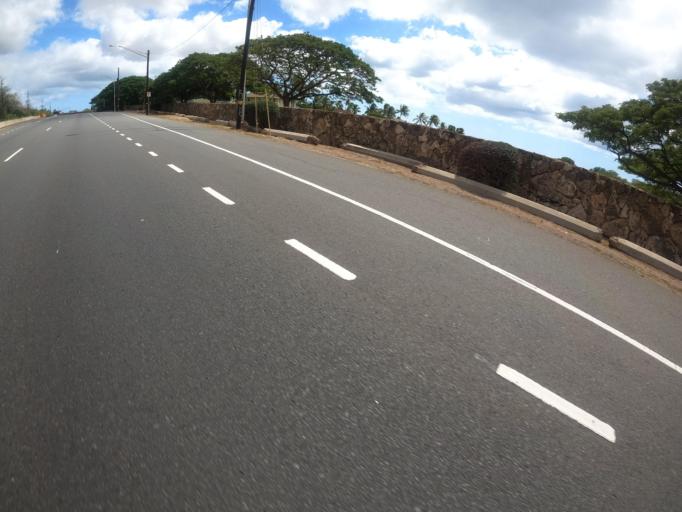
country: US
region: Hawaii
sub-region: Honolulu County
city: Makakilo
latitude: 21.3478
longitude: -158.1269
